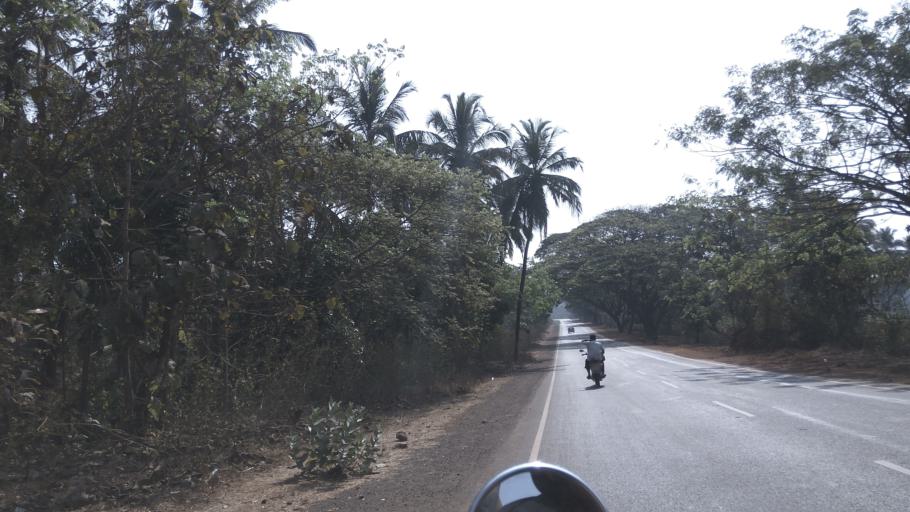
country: IN
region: Goa
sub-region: South Goa
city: Sanvordem
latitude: 15.3635
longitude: 74.1757
